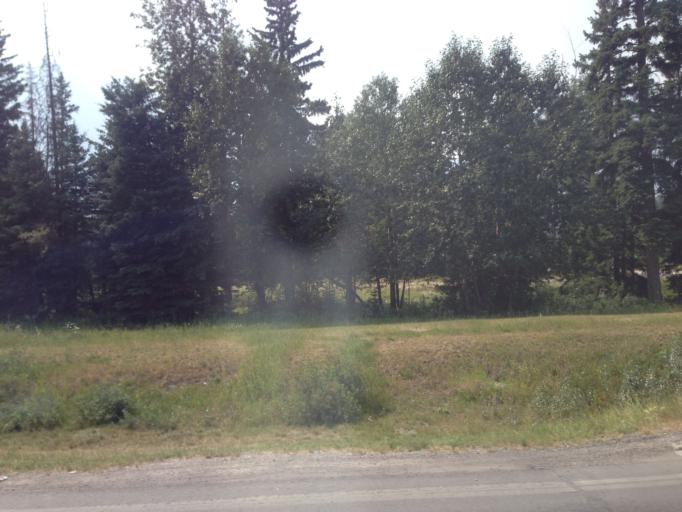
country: CA
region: Alberta
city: Canmore
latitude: 51.0843
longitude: -115.3441
